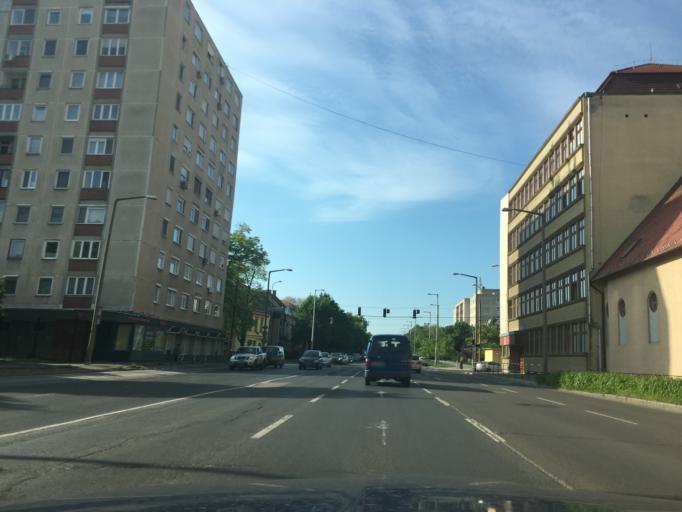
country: HU
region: Hajdu-Bihar
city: Debrecen
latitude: 47.5280
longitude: 21.6319
